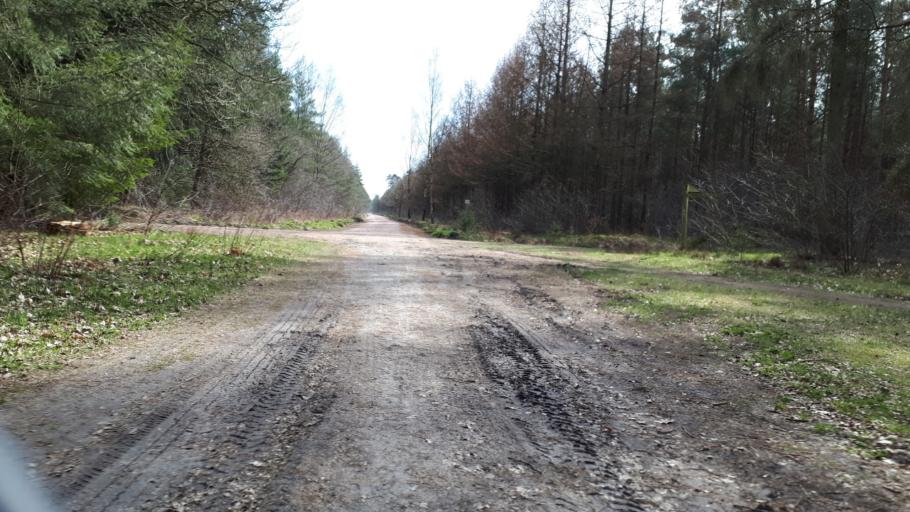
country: DE
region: Lower Saxony
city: Grossenkneten
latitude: 53.0337
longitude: 8.2834
